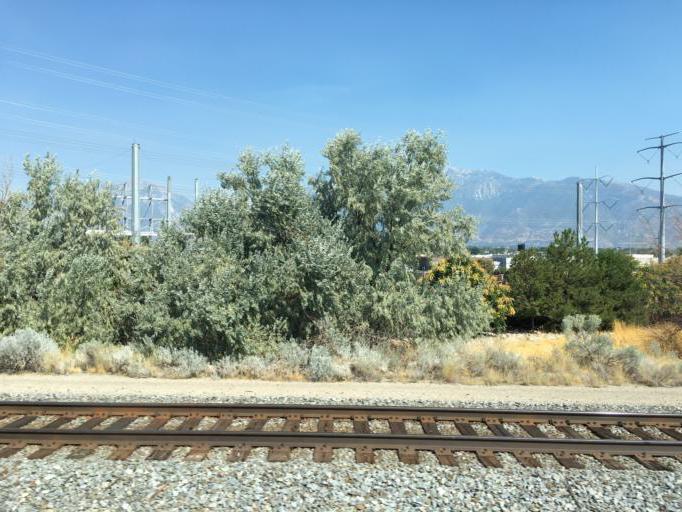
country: US
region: Utah
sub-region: Salt Lake County
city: South Jordan
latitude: 40.5560
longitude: -111.9016
